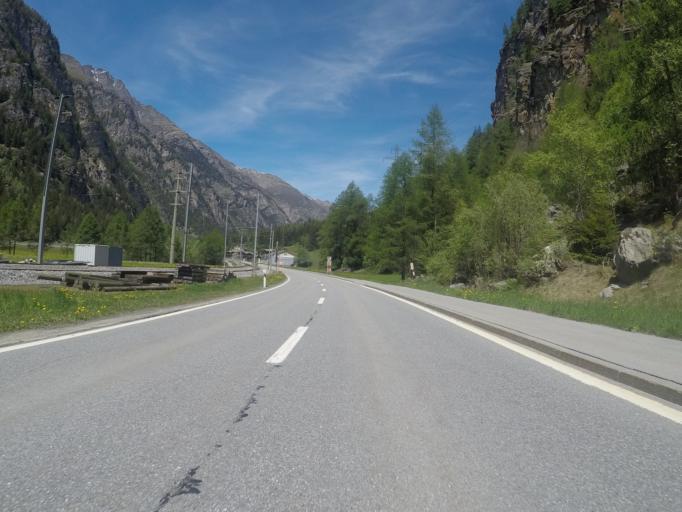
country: CH
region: Valais
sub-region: Visp District
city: Sankt Niklaus
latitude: 46.1408
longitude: 7.7934
